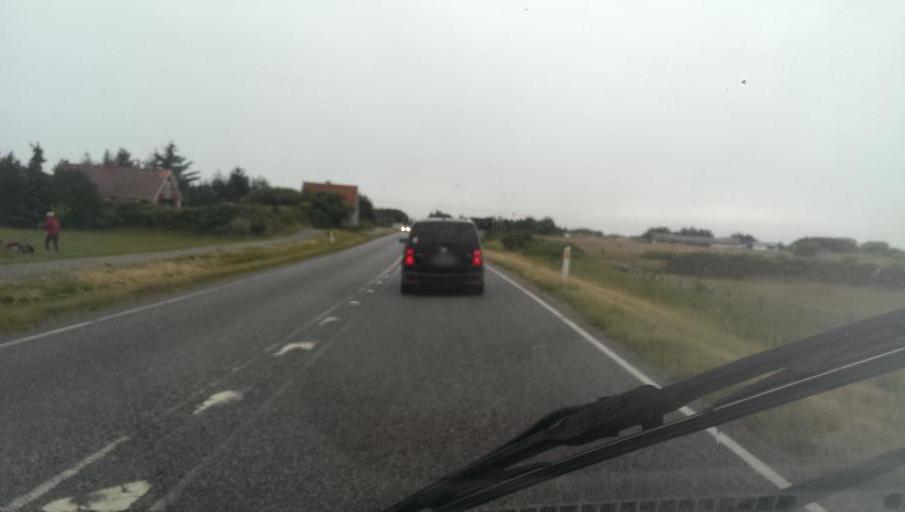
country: DK
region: Central Jutland
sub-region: Ringkobing-Skjern Kommune
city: Hvide Sande
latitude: 55.8657
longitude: 8.1816
